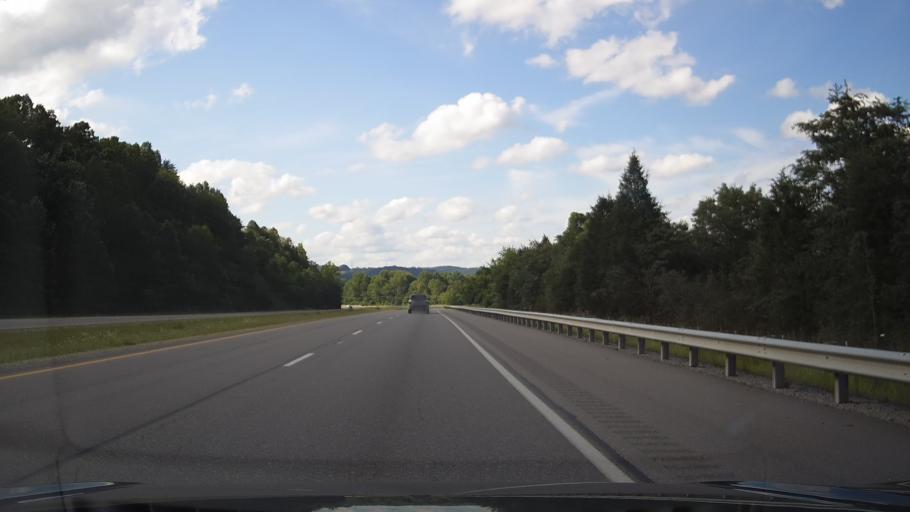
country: US
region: Kentucky
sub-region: Lawrence County
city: Louisa
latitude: 38.2136
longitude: -82.6042
